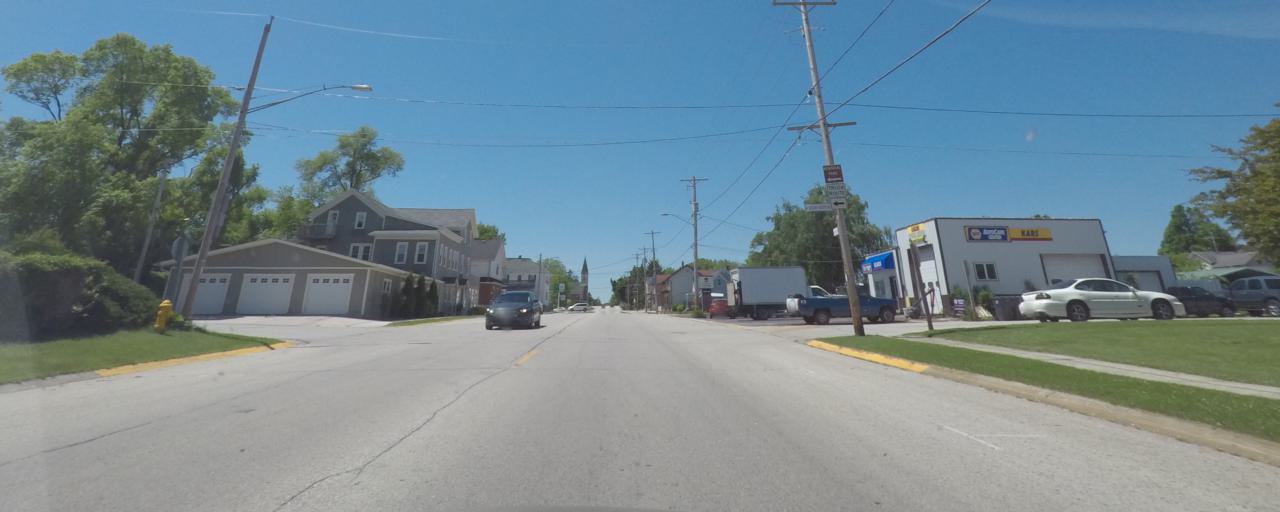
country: US
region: Wisconsin
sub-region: Sheboygan County
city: Plymouth
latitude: 43.6578
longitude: -88.0081
